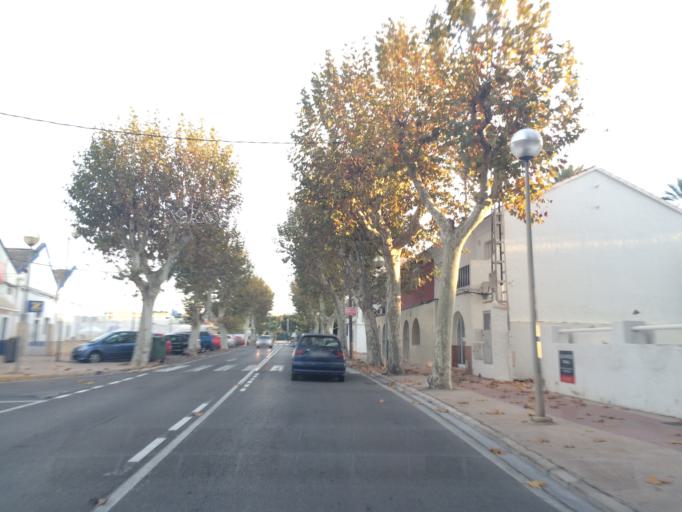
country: ES
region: Valencia
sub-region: Provincia de Alicante
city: Denia
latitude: 38.8402
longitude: 0.1137
